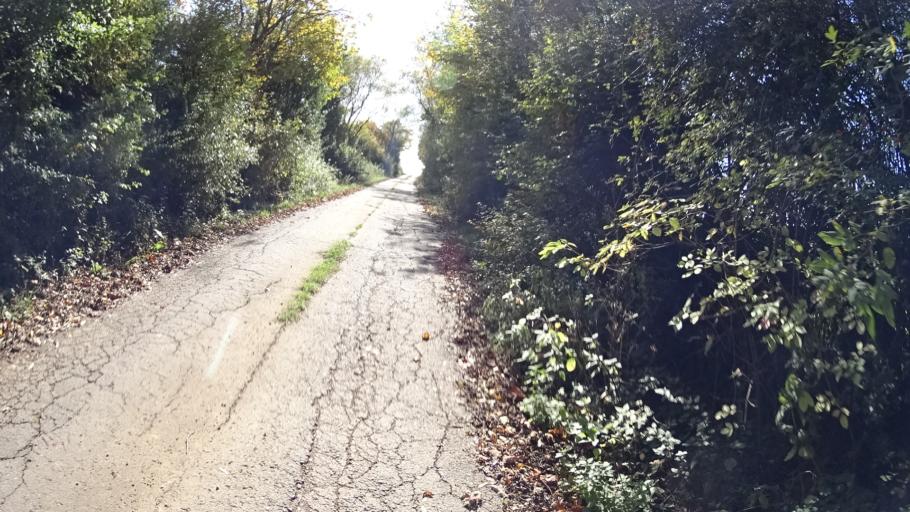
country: DE
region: Bavaria
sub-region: Upper Bavaria
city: Hitzhofen
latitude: 48.8627
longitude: 11.3338
